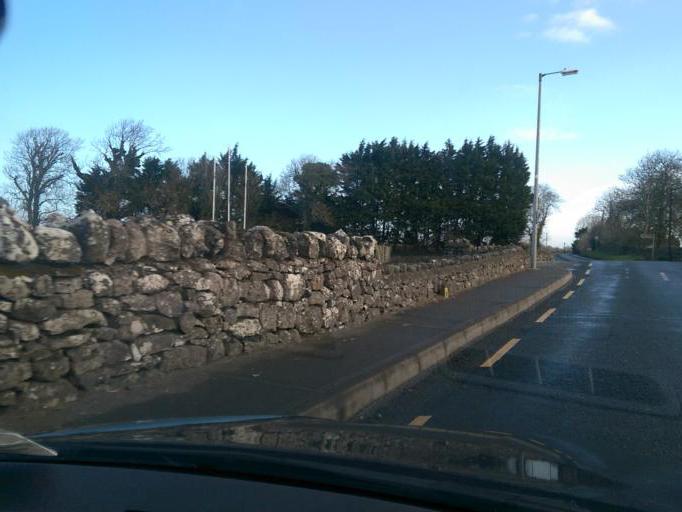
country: IE
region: Connaught
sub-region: County Galway
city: Athenry
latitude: 53.3771
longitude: -8.6982
